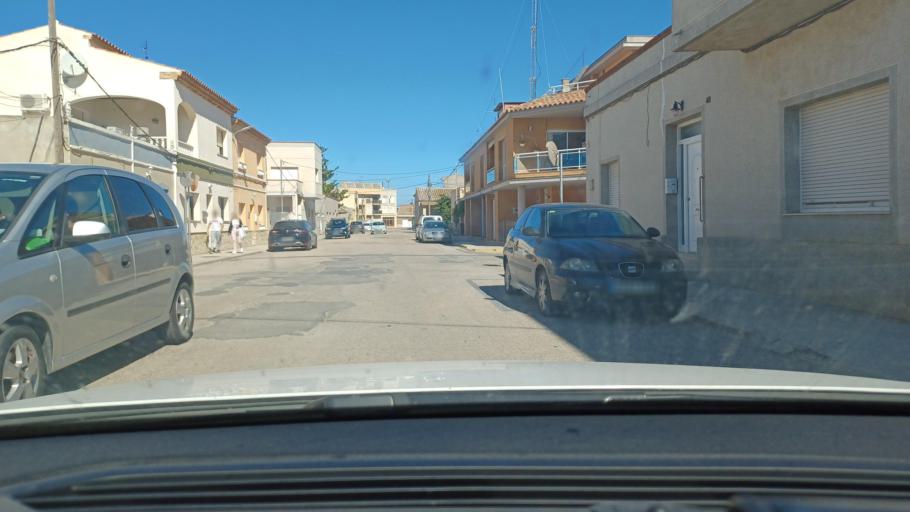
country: ES
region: Catalonia
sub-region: Provincia de Tarragona
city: Deltebre
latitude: 40.7188
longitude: 0.7397
